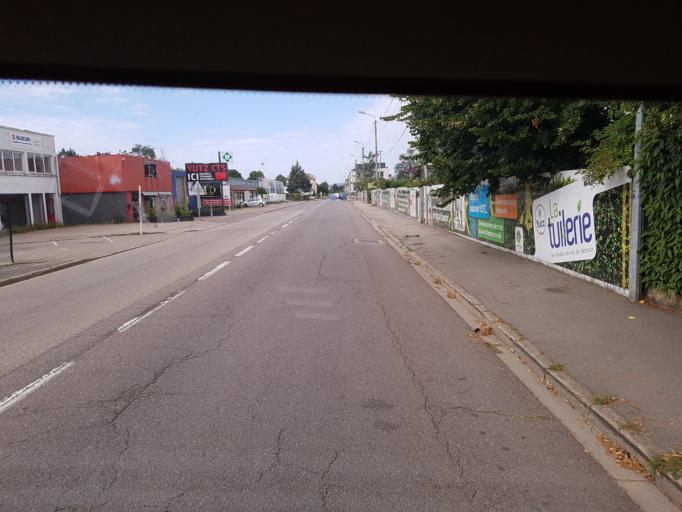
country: FR
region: Lorraine
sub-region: Departement de la Moselle
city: Yutz
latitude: 49.3645
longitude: 6.2024
